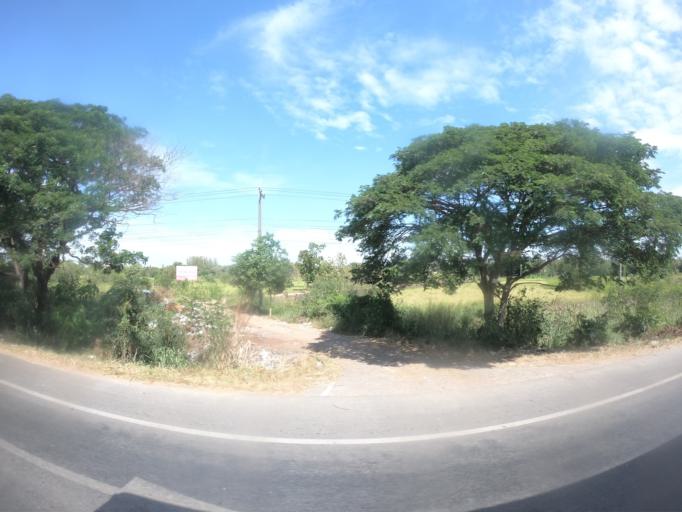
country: TH
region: Khon Kaen
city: Khon Kaen
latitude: 16.3953
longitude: 102.8553
